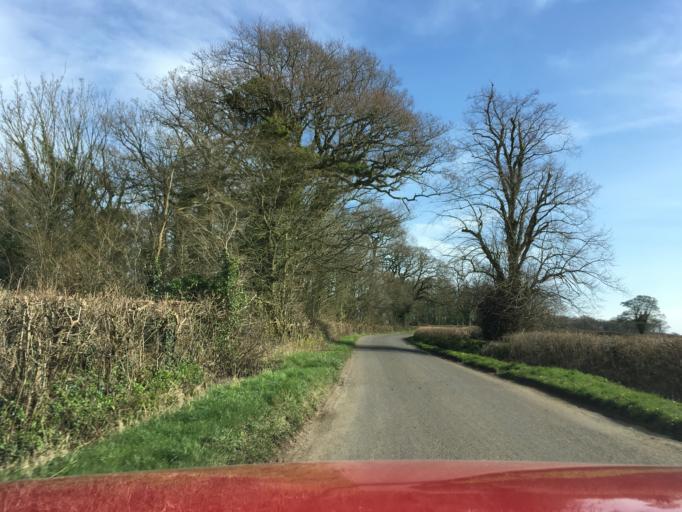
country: GB
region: England
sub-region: Wiltshire
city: Luckington
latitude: 51.5445
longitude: -2.2245
